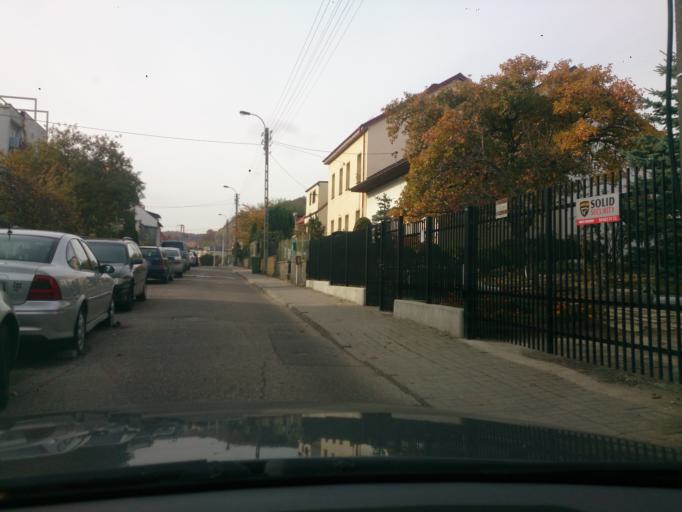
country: PL
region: Pomeranian Voivodeship
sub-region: Gdynia
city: Gdynia
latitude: 54.4865
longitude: 18.5245
